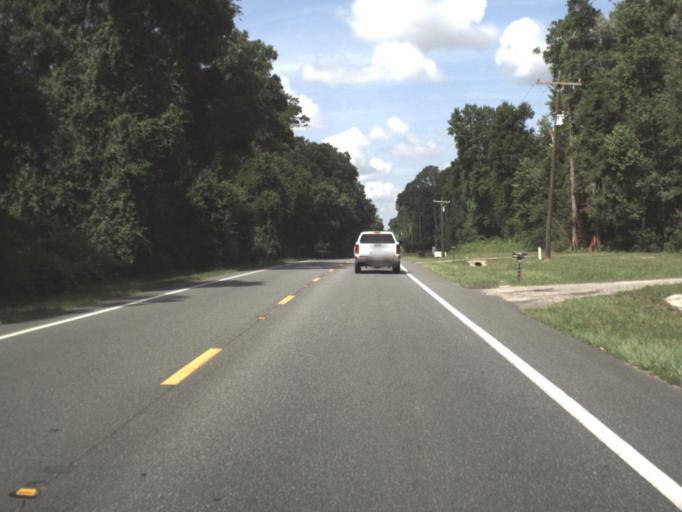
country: US
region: Florida
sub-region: Alachua County
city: Archer
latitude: 29.5476
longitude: -82.5012
